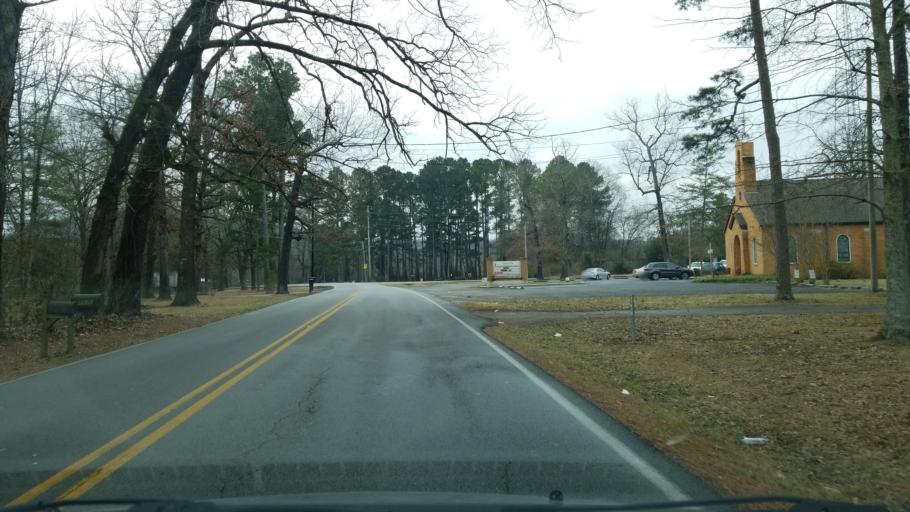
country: US
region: Tennessee
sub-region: Hamilton County
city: East Brainerd
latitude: 34.9838
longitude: -85.1475
